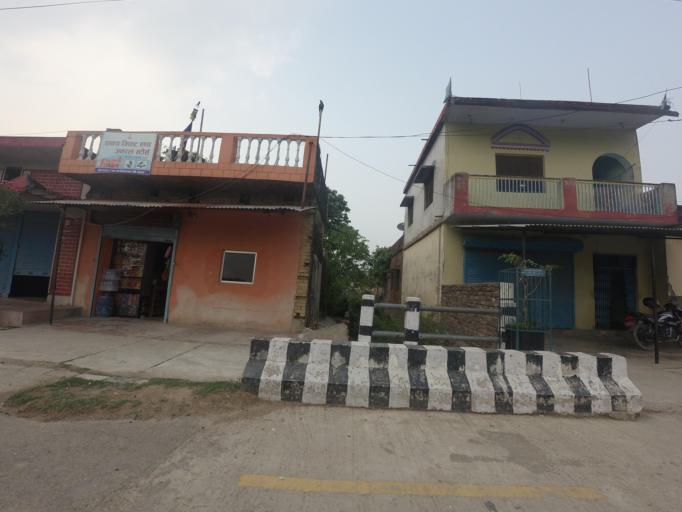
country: NP
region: Western Region
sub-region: Lumbini Zone
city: Bhairahawa
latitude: 27.5082
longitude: 83.4249
